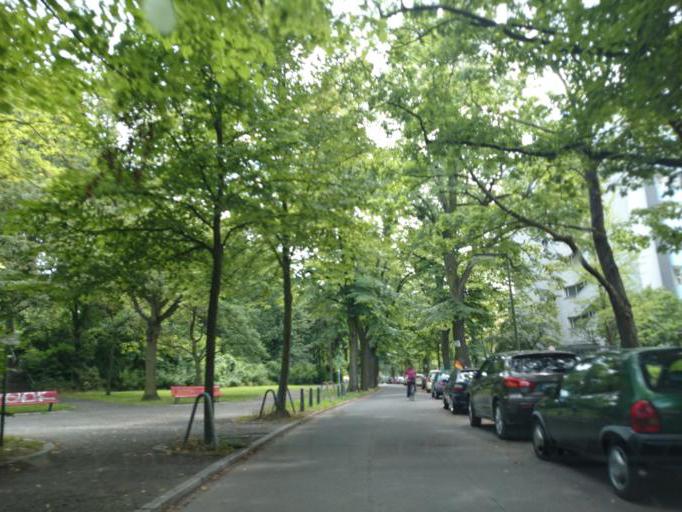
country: DE
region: Berlin
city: Lankwitz
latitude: 52.4305
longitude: 13.3484
